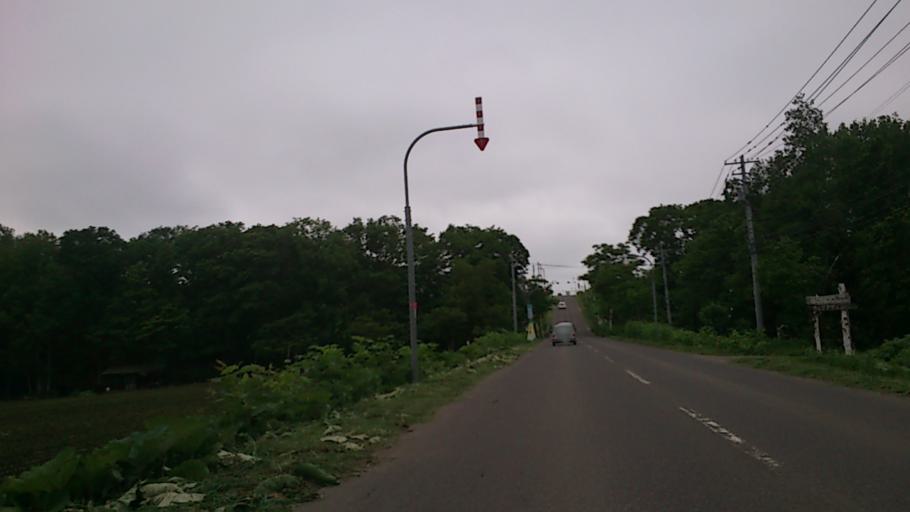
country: JP
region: Hokkaido
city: Niseko Town
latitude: 42.8336
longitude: 140.7038
